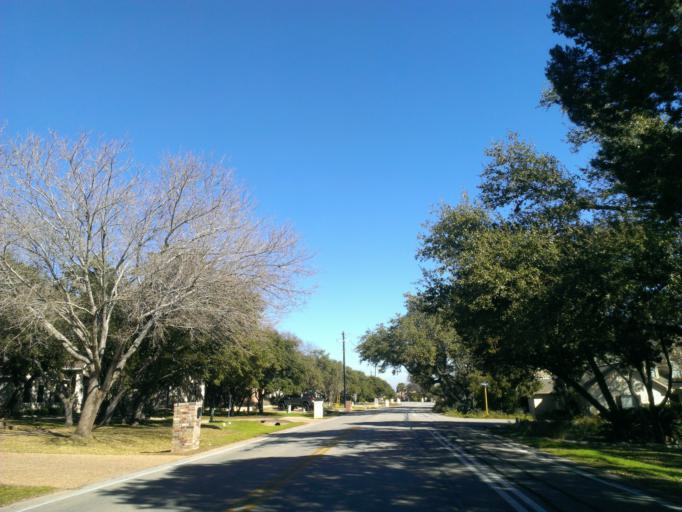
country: US
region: Texas
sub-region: Travis County
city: Lakeway
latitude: 30.3733
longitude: -97.9712
